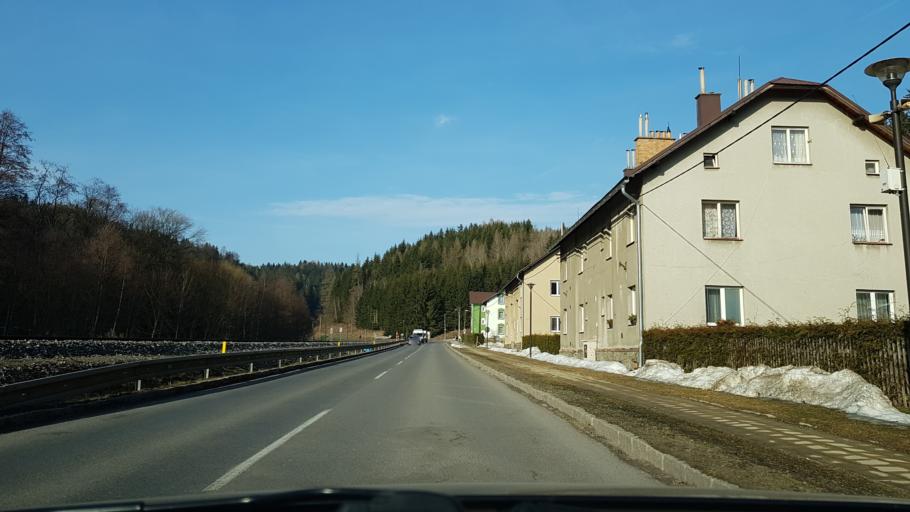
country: CZ
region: Olomoucky
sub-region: Okres Sumperk
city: Hanusovice
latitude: 50.1018
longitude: 16.9947
